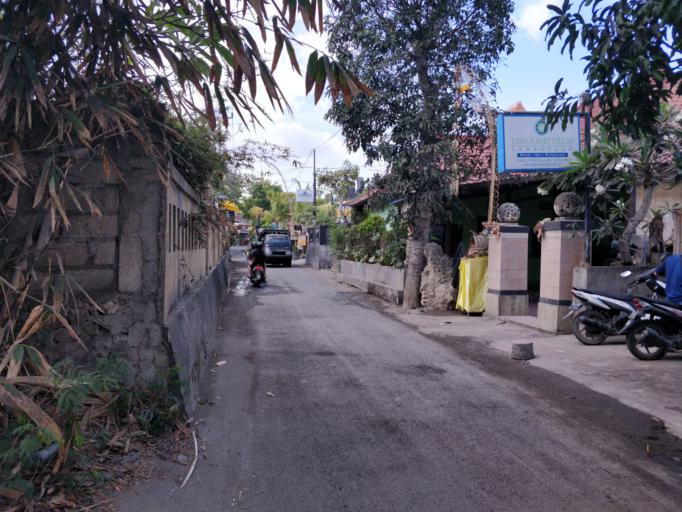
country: ID
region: Bali
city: Lembongan Kawan
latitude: -8.6864
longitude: 115.4364
